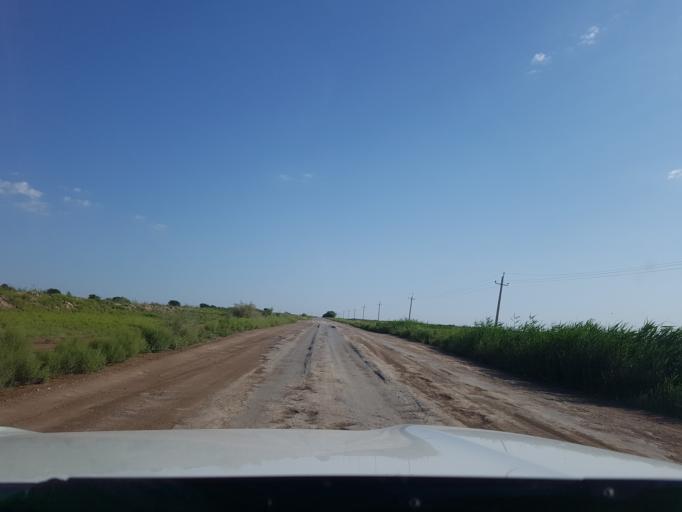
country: TM
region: Dasoguz
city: Koeneuergench
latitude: 41.9254
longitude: 58.7126
